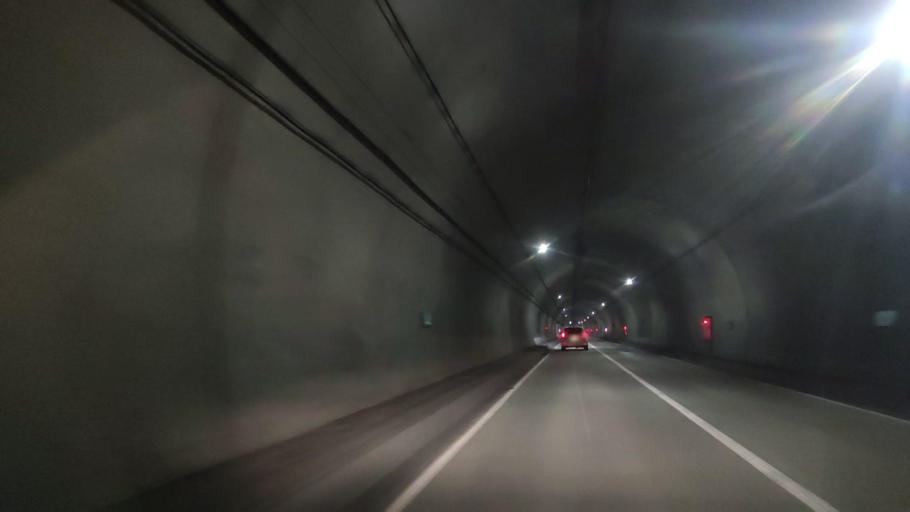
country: JP
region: Hokkaido
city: Rumoi
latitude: 43.7146
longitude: 141.3303
